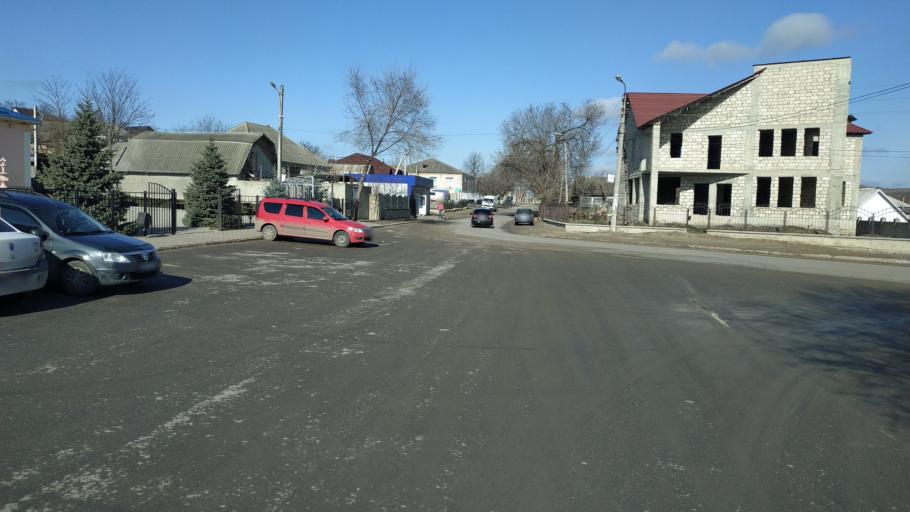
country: MD
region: Hincesti
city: Hincesti
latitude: 46.9296
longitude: 28.6506
